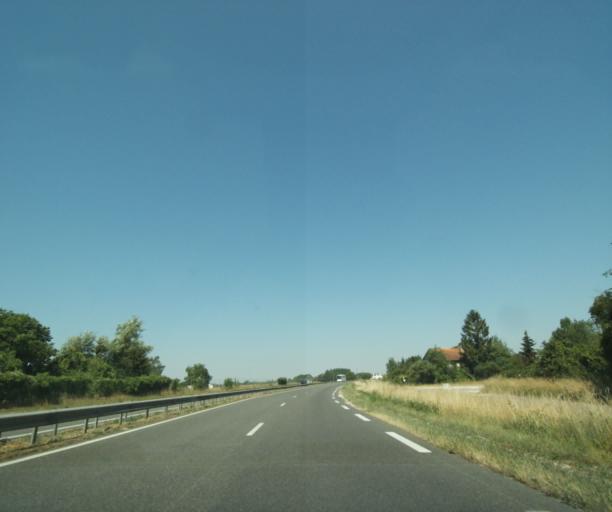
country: FR
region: Champagne-Ardenne
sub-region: Departement de la Haute-Marne
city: Villiers-en-Lieu
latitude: 48.6540
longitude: 4.8218
